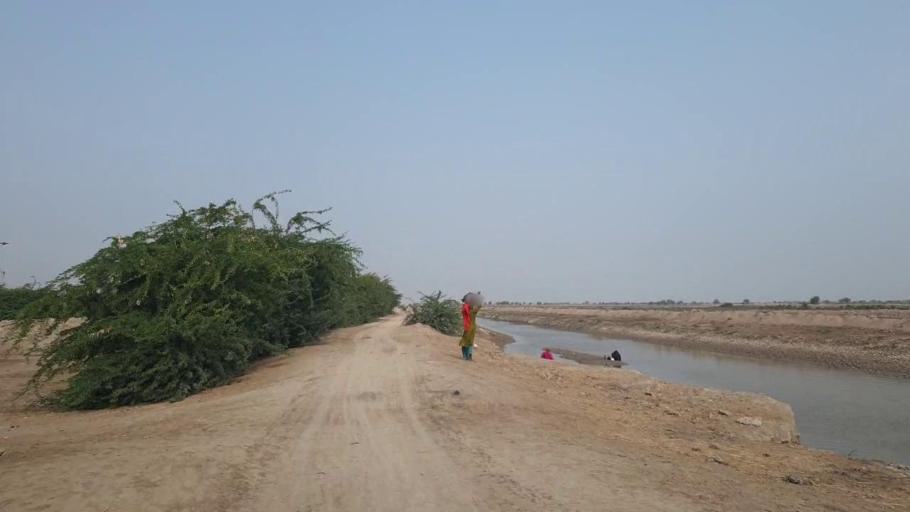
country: PK
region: Sindh
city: Badin
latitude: 24.7176
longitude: 68.7711
